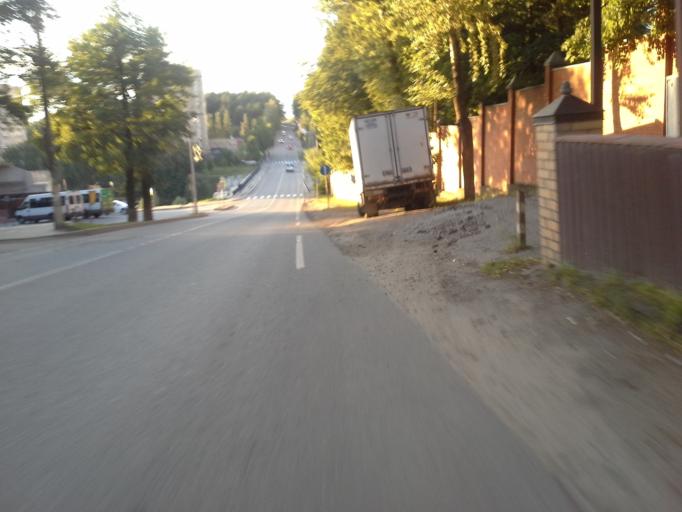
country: RU
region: Moskovskaya
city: Kommunarka
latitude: 55.5274
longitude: 37.4462
